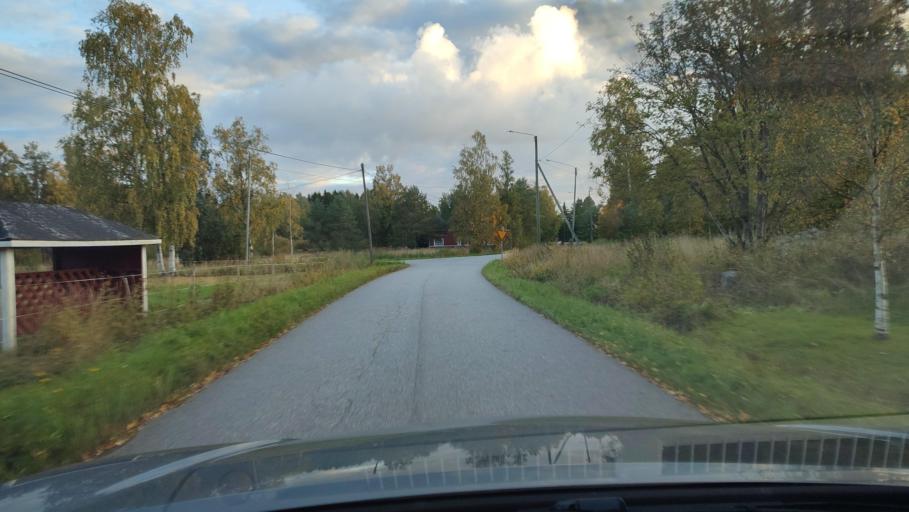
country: FI
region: Ostrobothnia
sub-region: Sydosterbotten
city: Kristinestad
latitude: 62.2440
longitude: 21.5150
